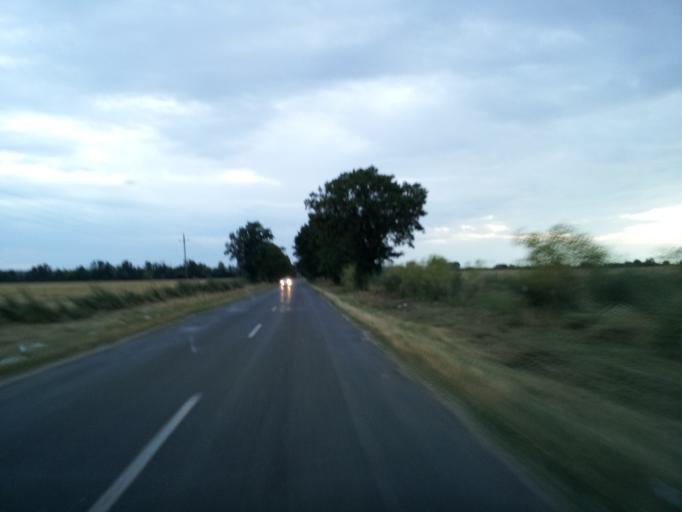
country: HU
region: Somogy
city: Adand
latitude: 46.8467
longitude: 18.1298
